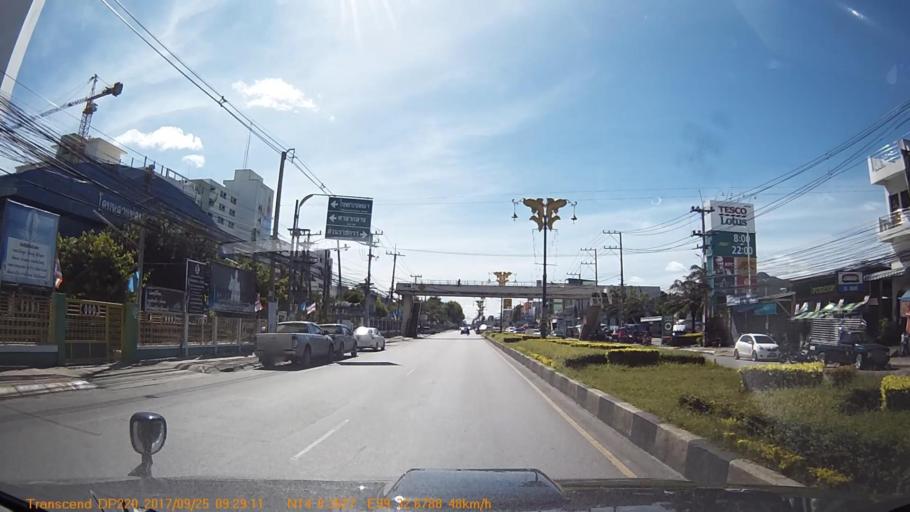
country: TH
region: Kanchanaburi
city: Kanchanaburi
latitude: 14.0059
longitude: 99.5448
